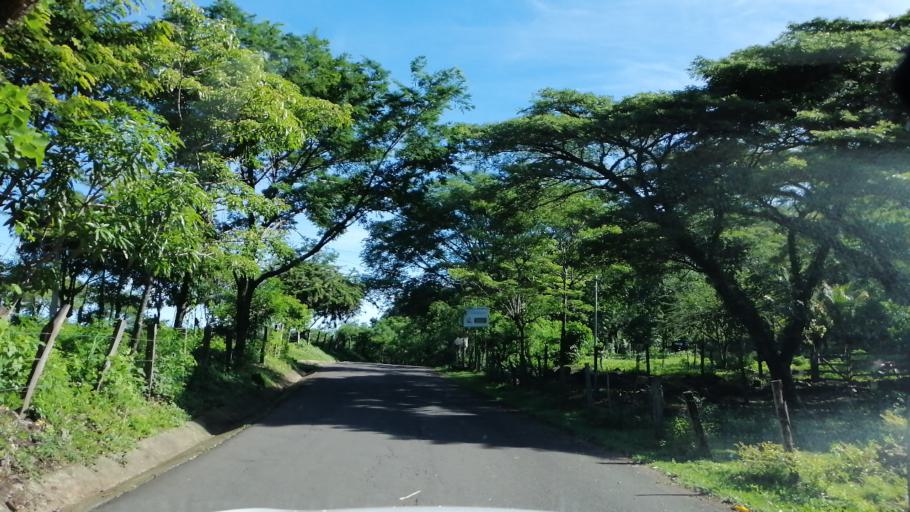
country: SV
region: Morazan
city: Corinto
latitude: 13.8023
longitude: -88.0038
